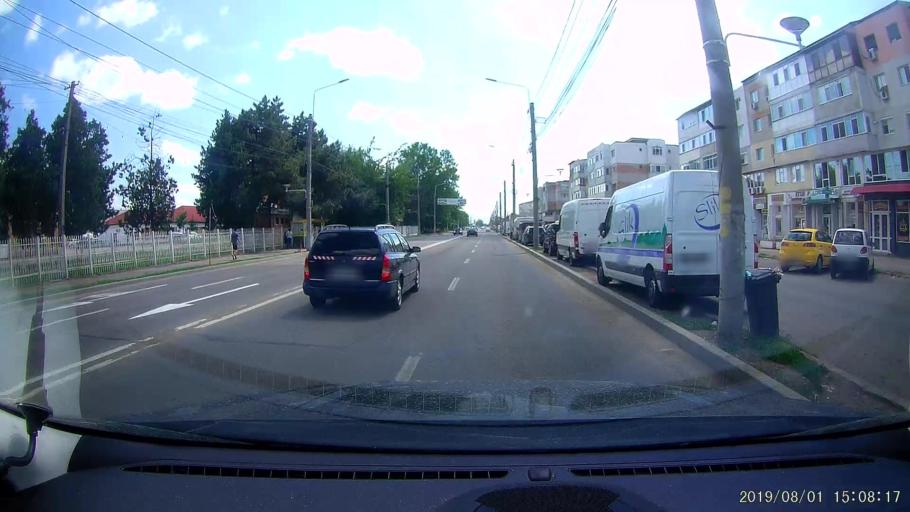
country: RO
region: Braila
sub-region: Municipiul Braila
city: Braila
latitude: 45.2428
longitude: 27.9466
